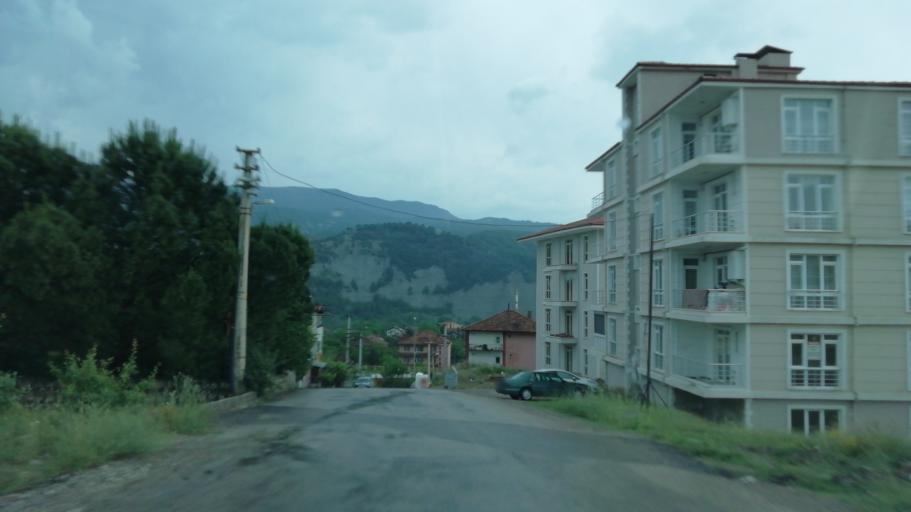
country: TR
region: Karabuk
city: Safranbolu
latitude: 41.2198
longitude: 32.6860
